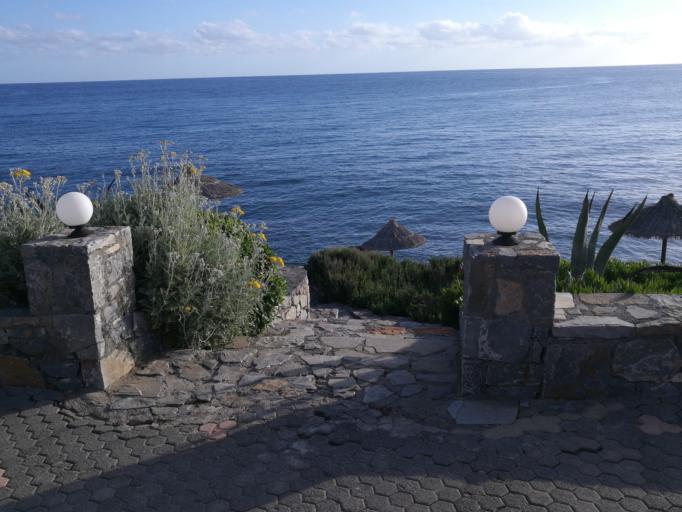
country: GR
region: Crete
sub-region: Nomos Irakleiou
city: Stalis
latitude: 35.3033
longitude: 25.4228
